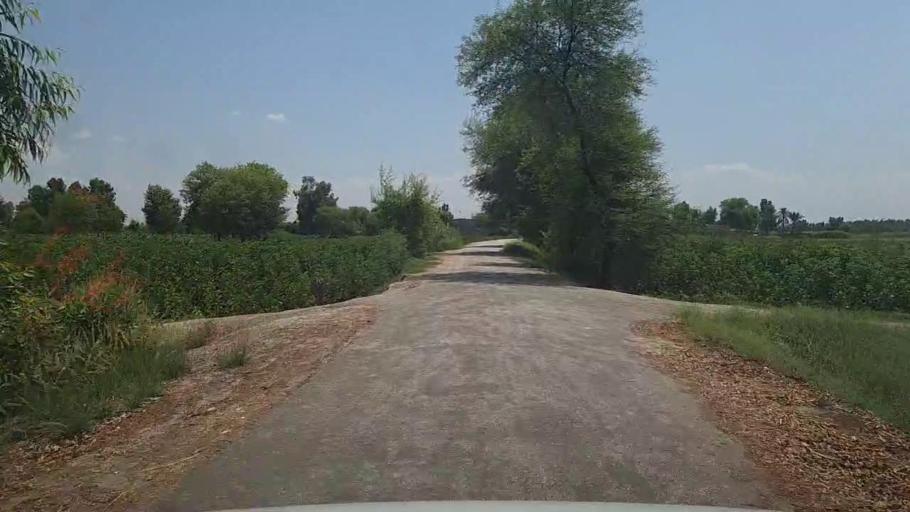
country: PK
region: Sindh
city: Ubauro
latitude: 28.1570
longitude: 69.7486
